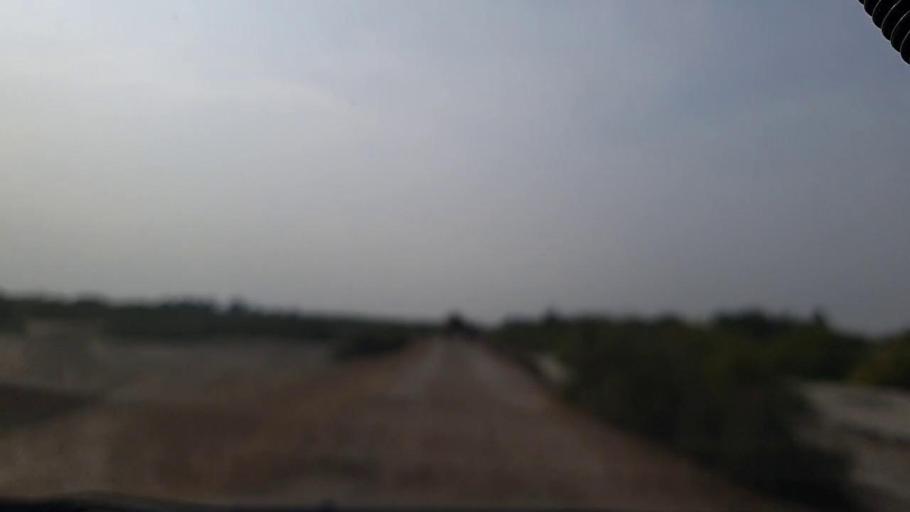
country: PK
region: Sindh
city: Thatta
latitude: 24.6134
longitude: 67.9559
